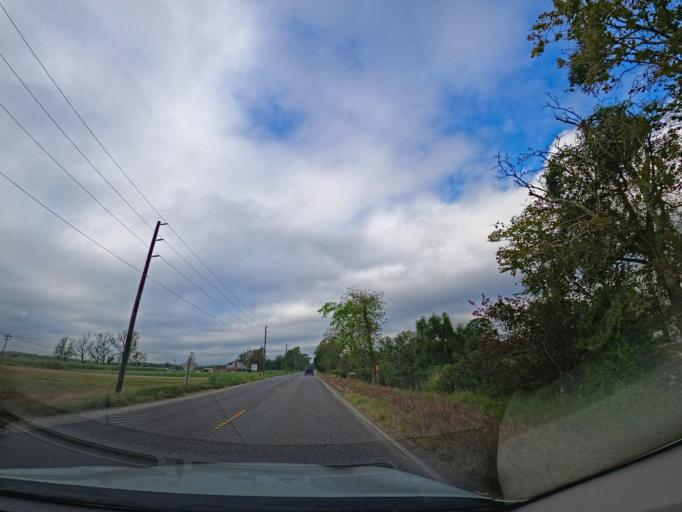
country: US
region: Louisiana
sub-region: Terrebonne Parish
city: Bayou Cane
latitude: 29.6074
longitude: -90.8624
